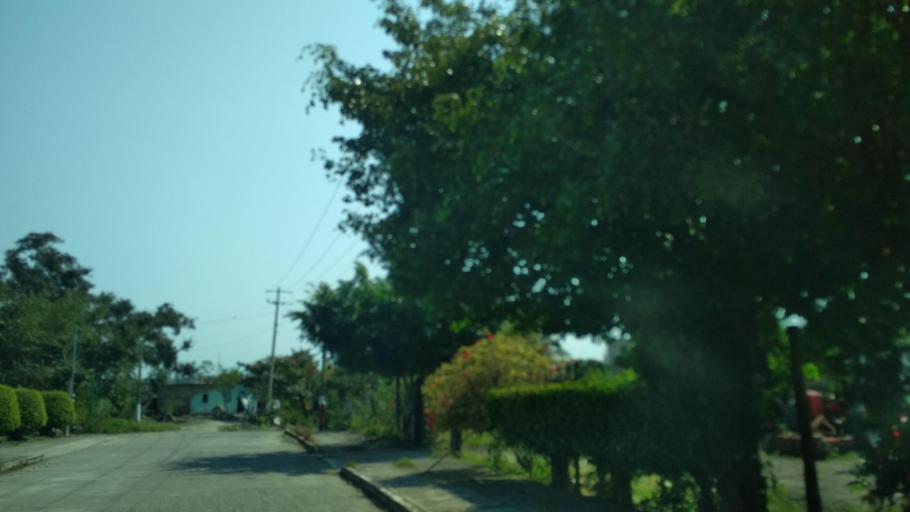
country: MX
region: Veracruz
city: Gutierrez Zamora
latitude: 20.4145
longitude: -97.1872
